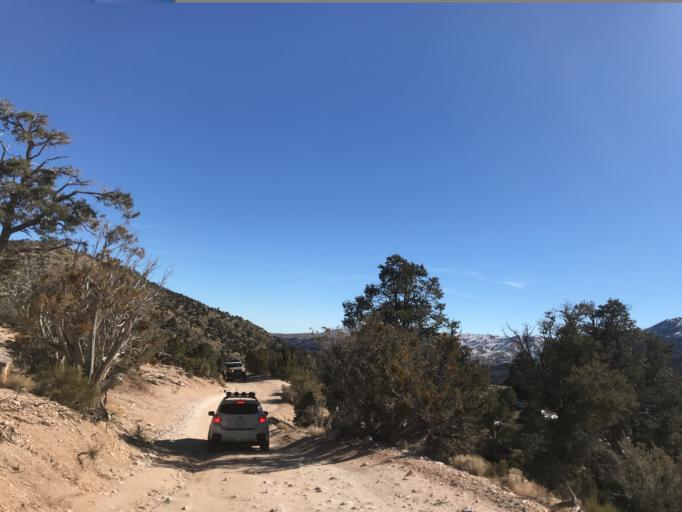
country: US
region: California
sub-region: San Bernardino County
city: Big Bear City
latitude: 34.2405
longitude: -116.6926
